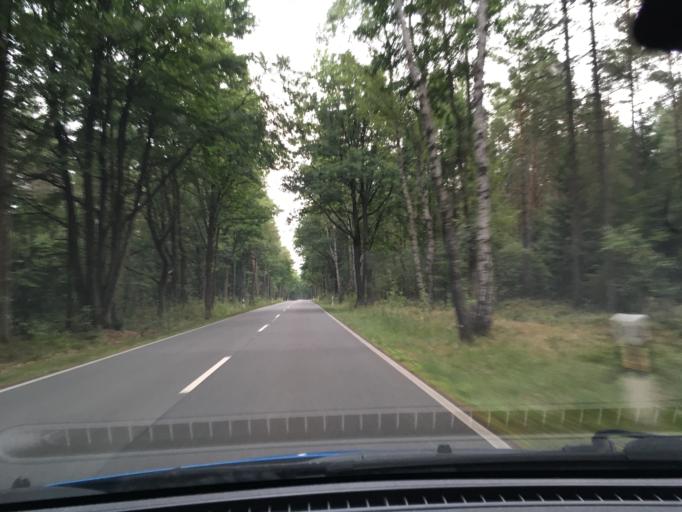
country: DE
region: Lower Saxony
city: Scharnhorst
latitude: 52.7701
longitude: 10.3034
